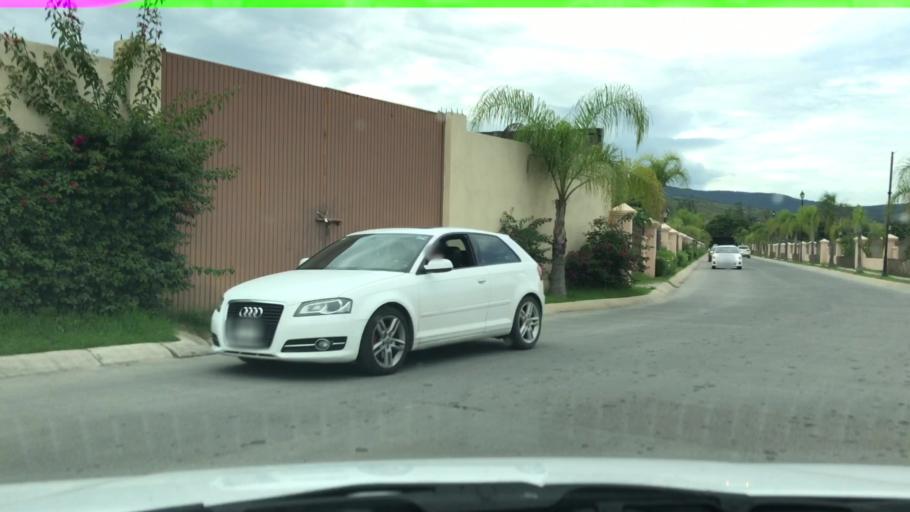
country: MX
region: Jalisco
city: Nicolas R Casillas
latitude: 20.5411
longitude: -103.4877
